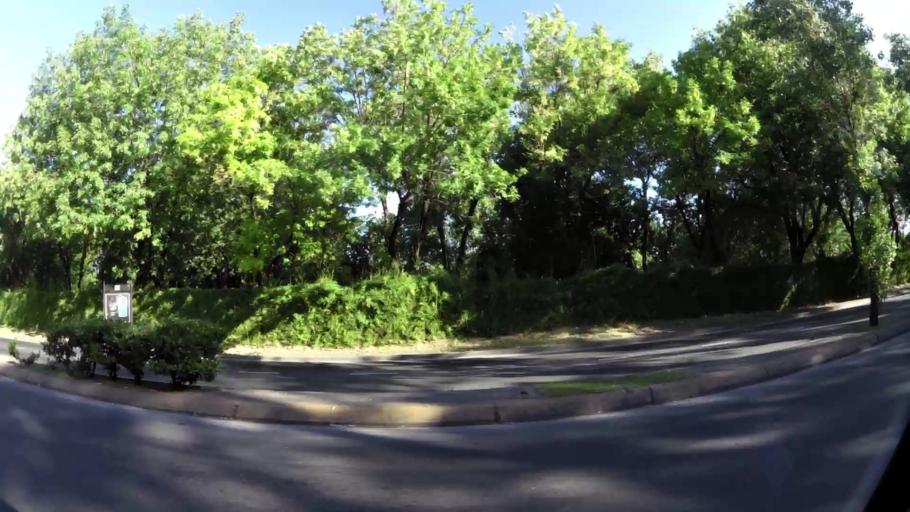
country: AR
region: Buenos Aires
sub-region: Partido de San Isidro
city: San Isidro
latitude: -34.4890
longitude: -58.5410
